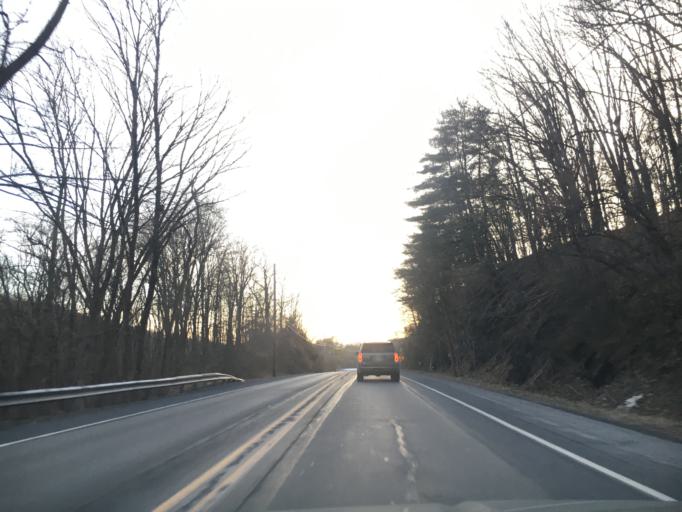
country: US
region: Pennsylvania
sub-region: Monroe County
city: East Stroudsburg
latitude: 41.0115
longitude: -75.1320
